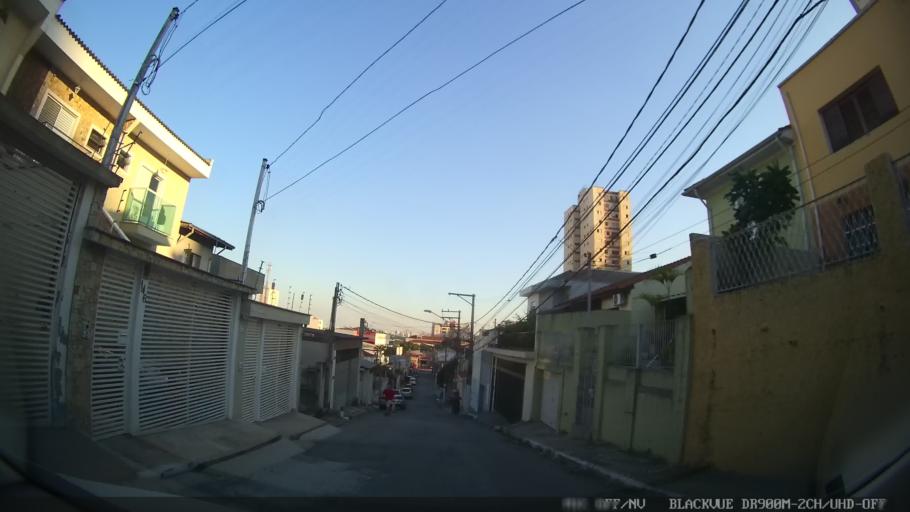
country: BR
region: Sao Paulo
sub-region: Sao Paulo
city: Sao Paulo
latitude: -23.4989
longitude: -46.6346
